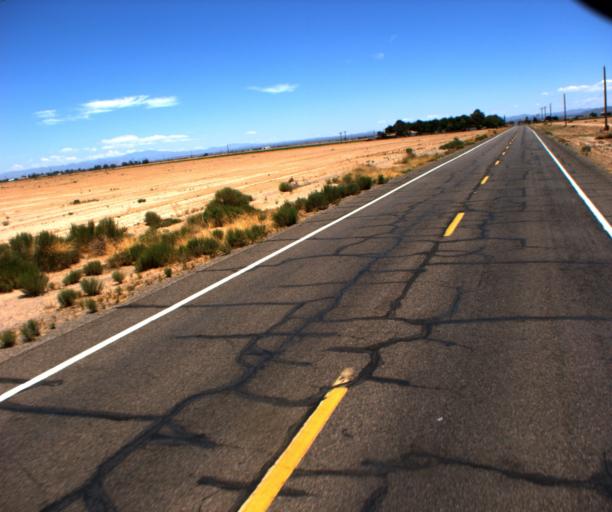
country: US
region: Arizona
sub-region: Pinal County
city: Coolidge
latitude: 32.8795
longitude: -111.5540
